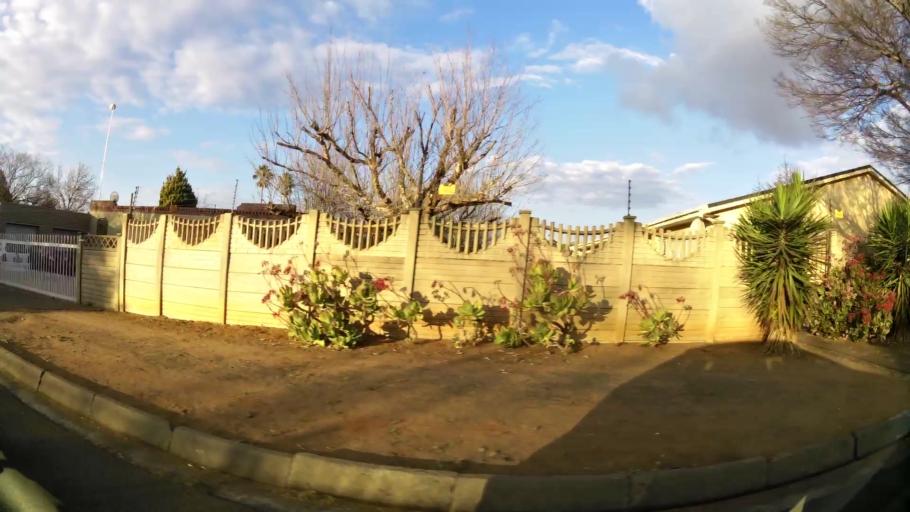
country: ZA
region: Orange Free State
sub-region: Mangaung Metropolitan Municipality
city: Bloemfontein
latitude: -29.1357
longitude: 26.1850
